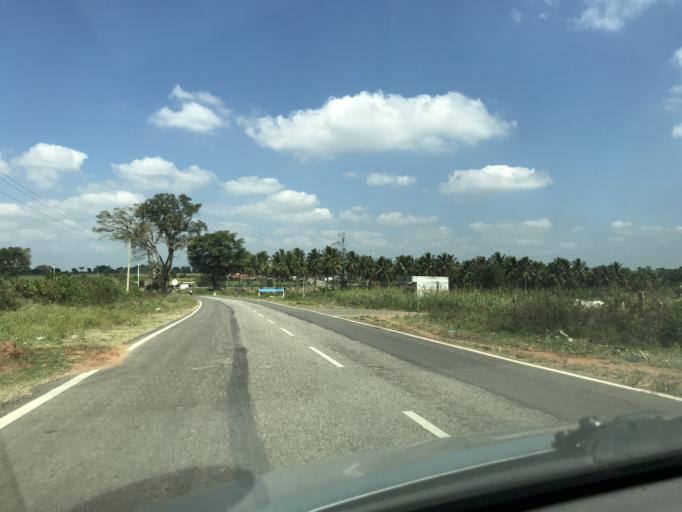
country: IN
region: Karnataka
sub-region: Mysore
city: Heggadadevankote
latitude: 12.1648
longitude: 76.2792
